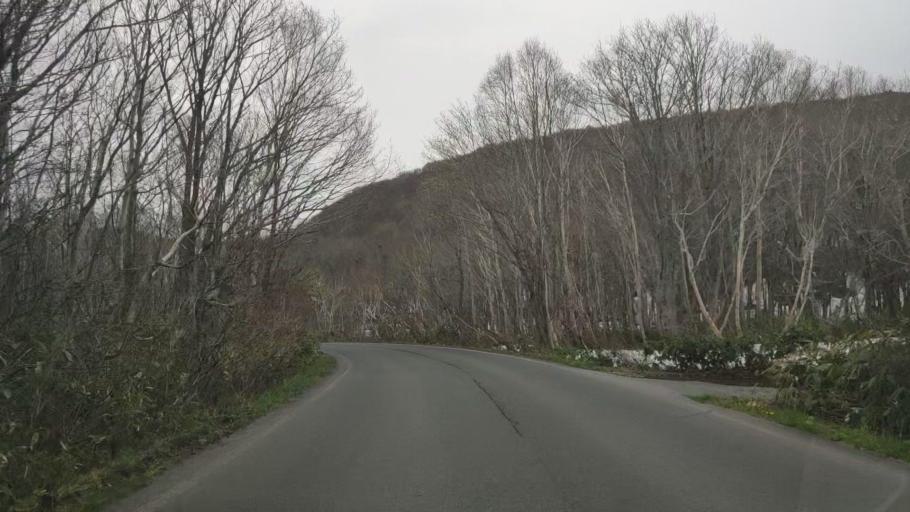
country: JP
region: Aomori
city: Aomori Shi
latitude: 40.6932
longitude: 140.9088
